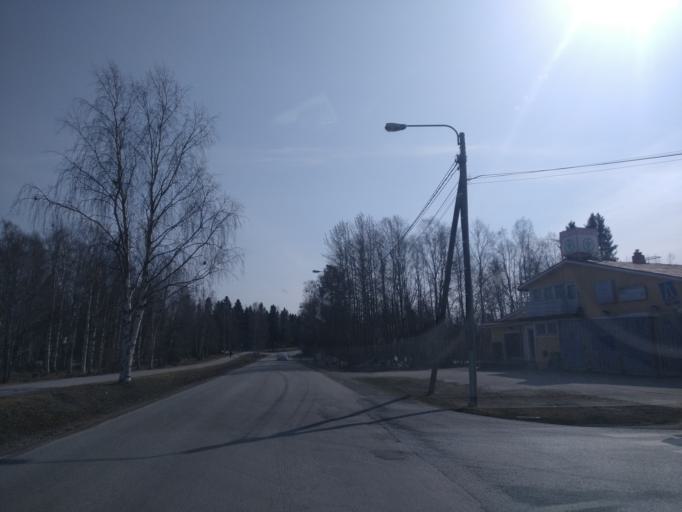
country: FI
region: Lapland
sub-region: Kemi-Tornio
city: Kemi
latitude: 65.7266
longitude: 24.6173
